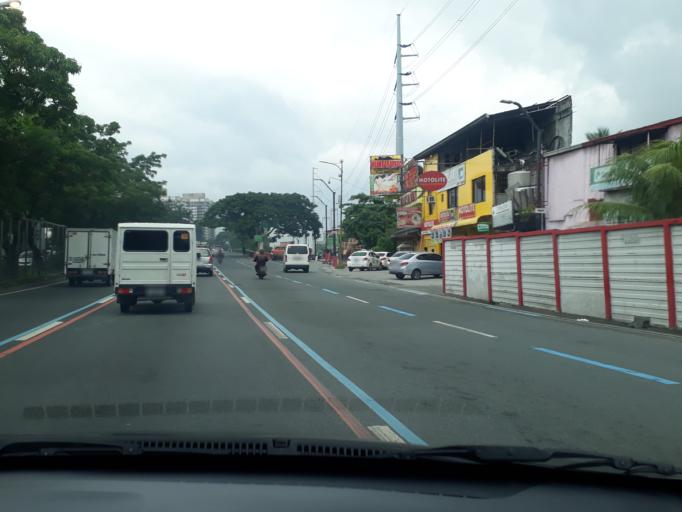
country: PH
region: Calabarzon
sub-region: Province of Rizal
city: Pateros
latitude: 14.5350
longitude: 121.0575
